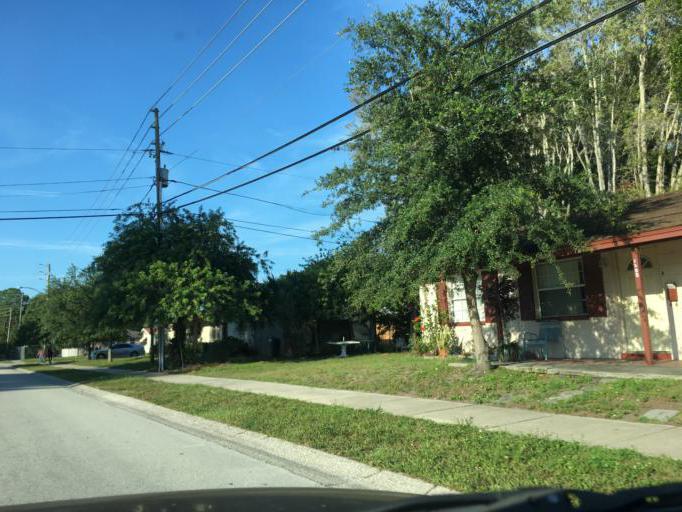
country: US
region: Florida
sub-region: Pinellas County
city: Pinellas Park
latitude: 27.8382
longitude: -82.7040
